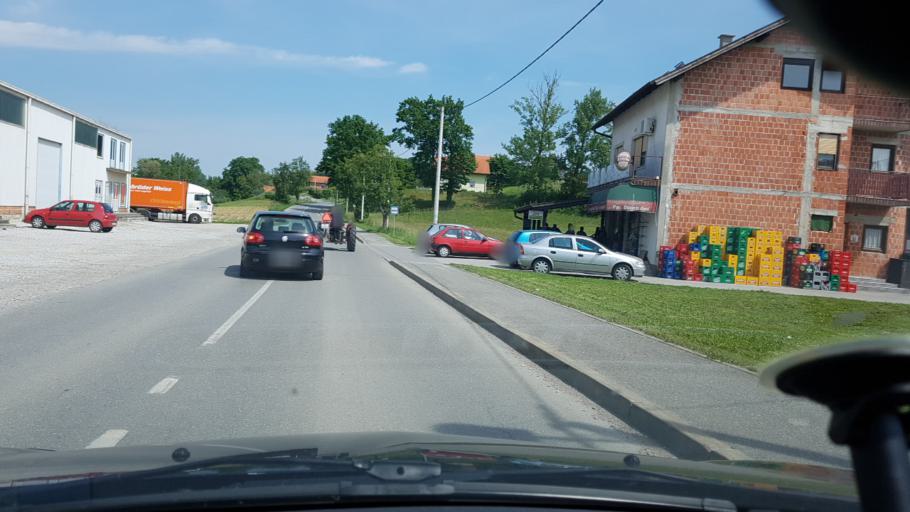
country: HR
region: Krapinsko-Zagorska
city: Zabok
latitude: 46.0692
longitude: 15.9237
